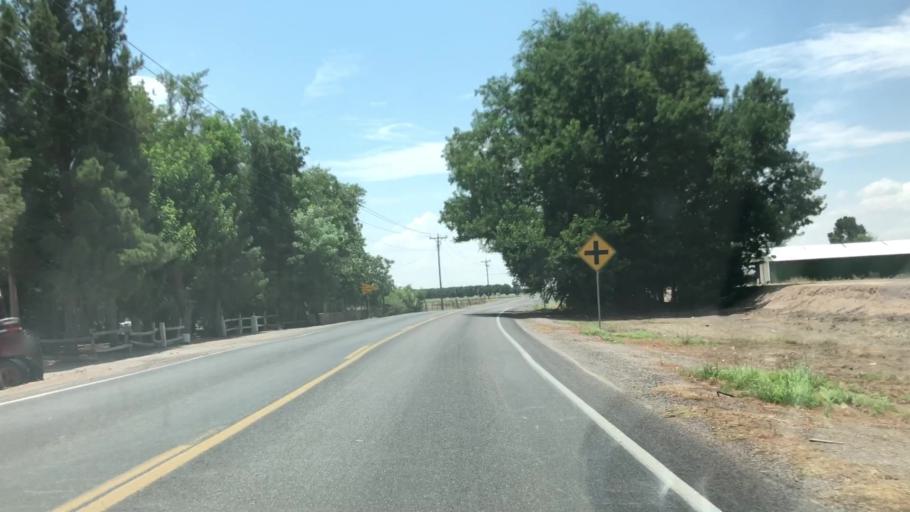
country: US
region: New Mexico
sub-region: Dona Ana County
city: Vado
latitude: 32.0844
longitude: -106.6834
